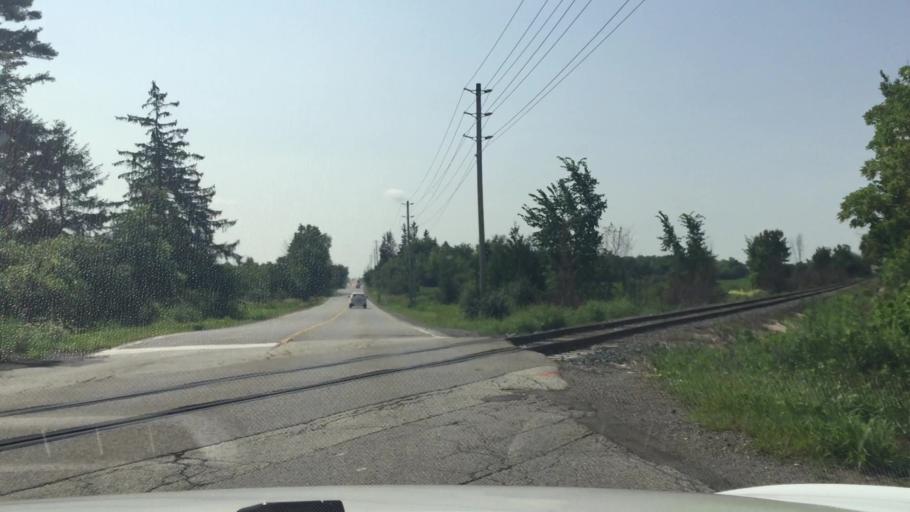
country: CA
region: Ontario
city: Pickering
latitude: 43.9056
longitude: -79.1927
